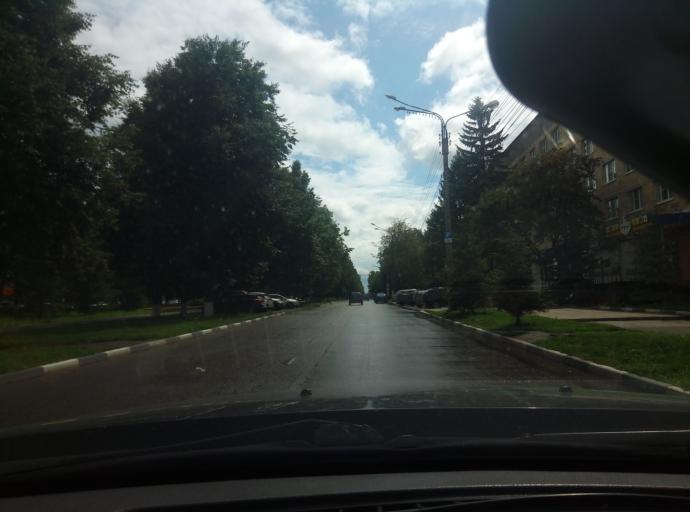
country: RU
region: Tula
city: Novomoskovsk
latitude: 54.0178
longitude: 38.2961
